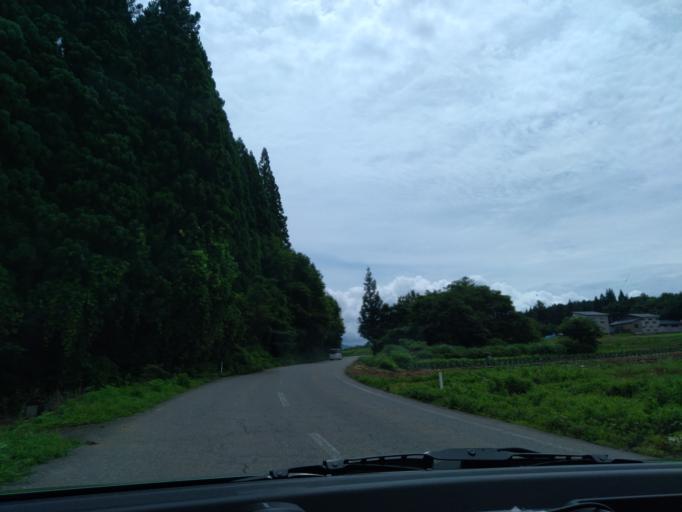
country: JP
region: Akita
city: Kakunodatemachi
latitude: 39.5809
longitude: 140.6249
